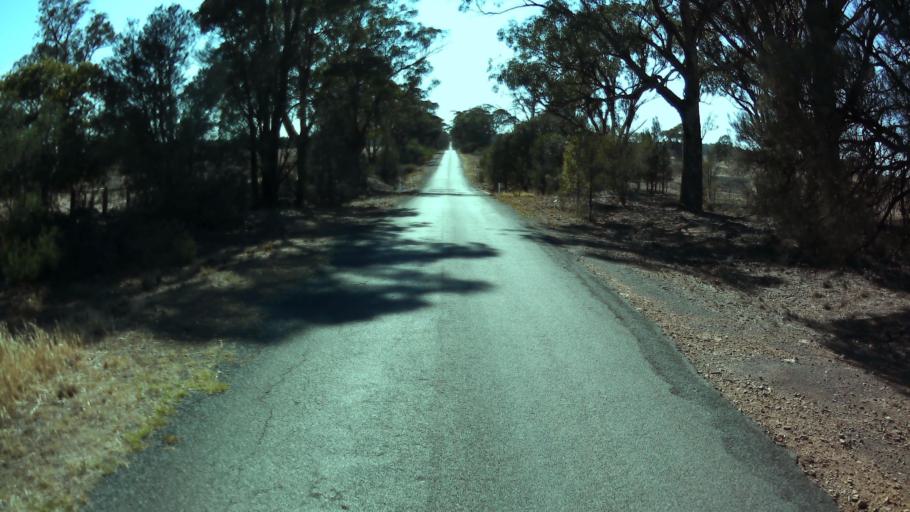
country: AU
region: New South Wales
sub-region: Weddin
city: Grenfell
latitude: -33.7827
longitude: 147.9682
